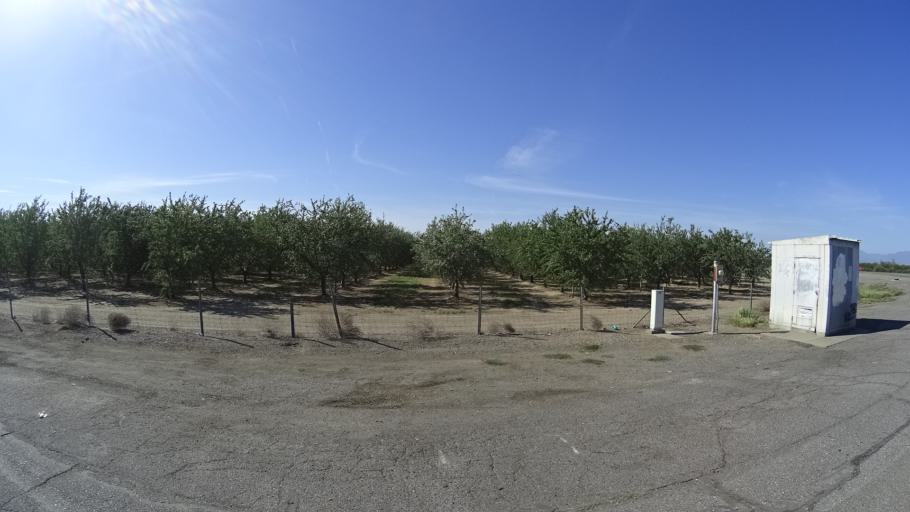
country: US
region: California
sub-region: Glenn County
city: Orland
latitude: 39.6824
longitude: -122.2026
